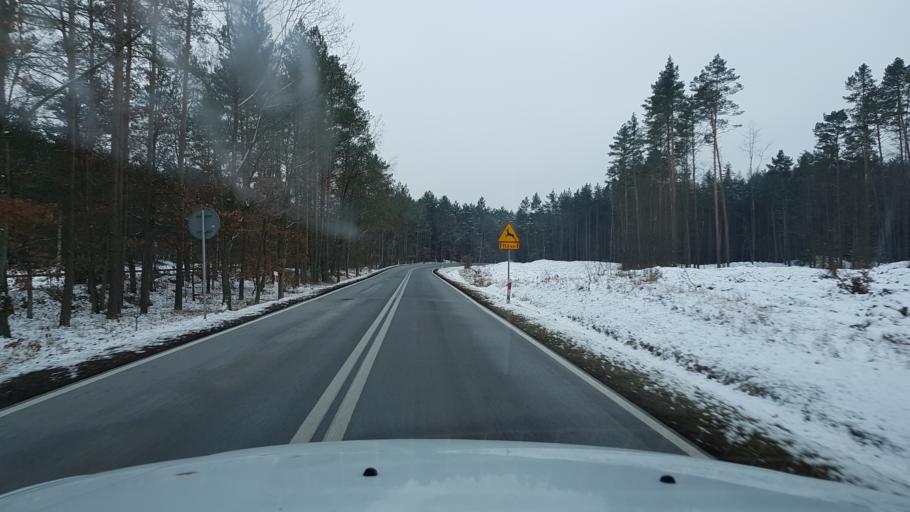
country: PL
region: West Pomeranian Voivodeship
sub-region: Powiat gryfinski
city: Widuchowa
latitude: 53.0648
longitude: 14.4598
